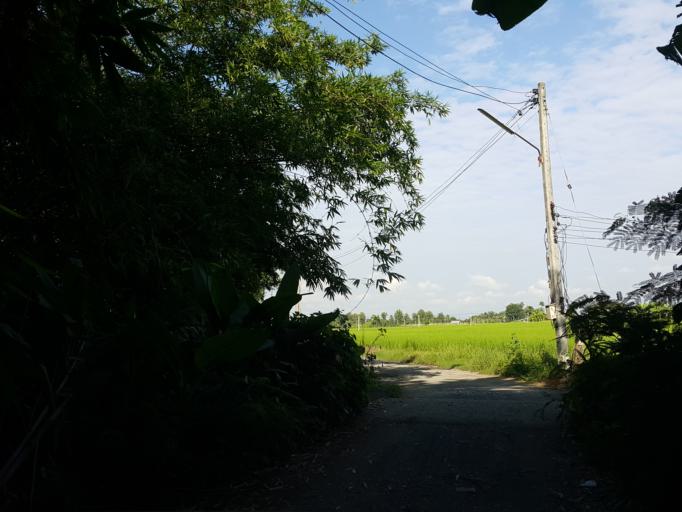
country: TH
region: Chiang Mai
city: San Kamphaeng
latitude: 18.8228
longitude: 99.1680
